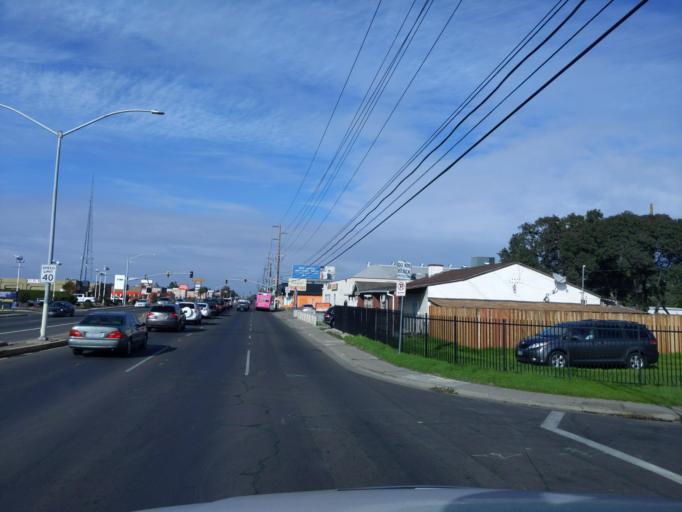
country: US
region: California
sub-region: San Joaquin County
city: August
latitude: 37.9869
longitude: -121.2848
